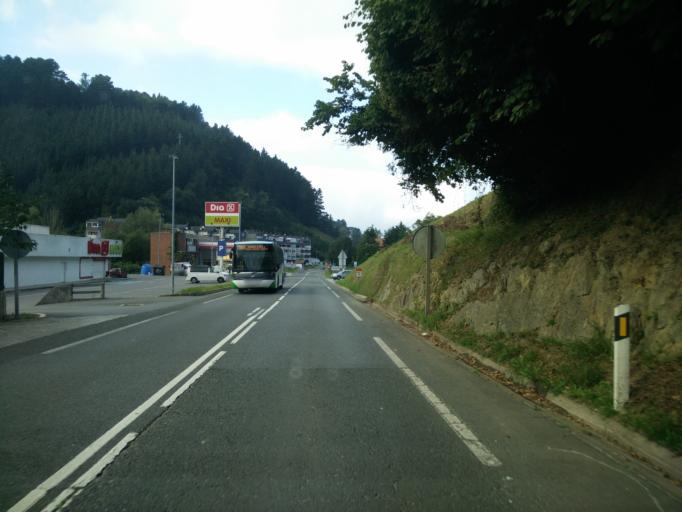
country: ES
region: Basque Country
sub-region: Bizkaia
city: Ondarroa
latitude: 43.3130
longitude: -2.4106
